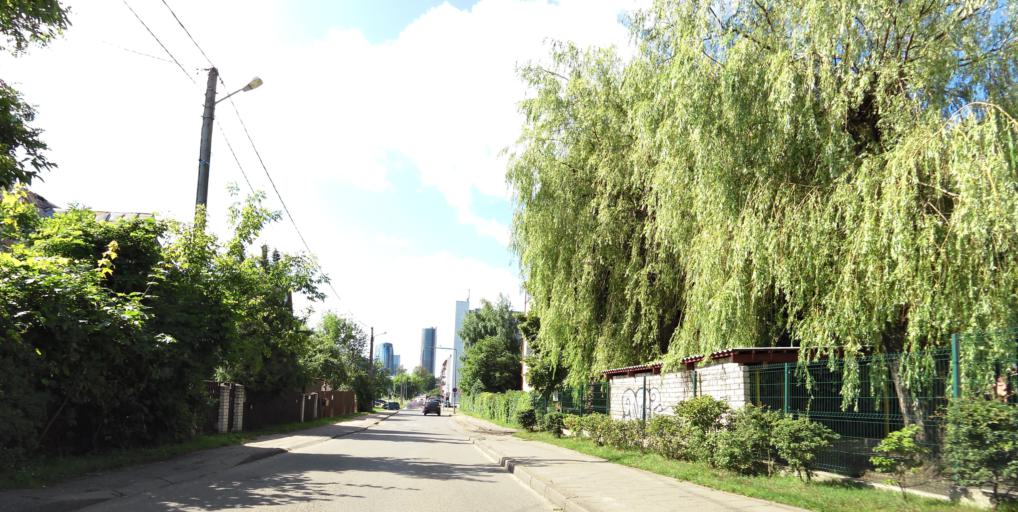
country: LT
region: Vilnius County
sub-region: Vilnius
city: Vilnius
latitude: 54.7050
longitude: 25.2802
